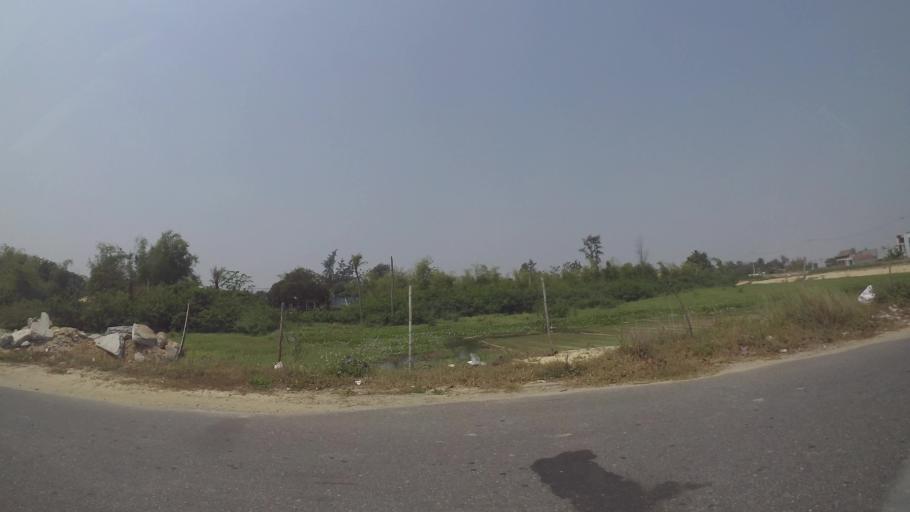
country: VN
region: Da Nang
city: Ngu Hanh Son
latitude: 15.9831
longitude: 108.2608
